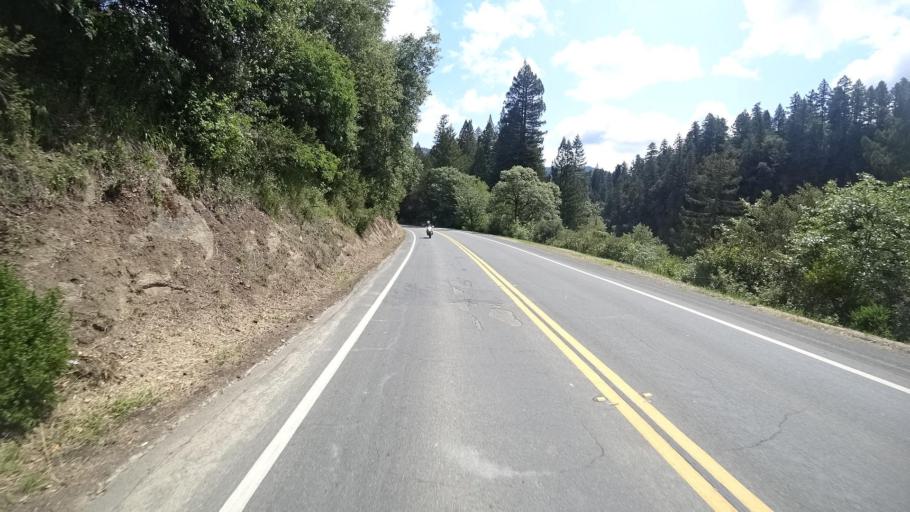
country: US
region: California
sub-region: Humboldt County
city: Redway
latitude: 40.1151
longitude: -123.8121
